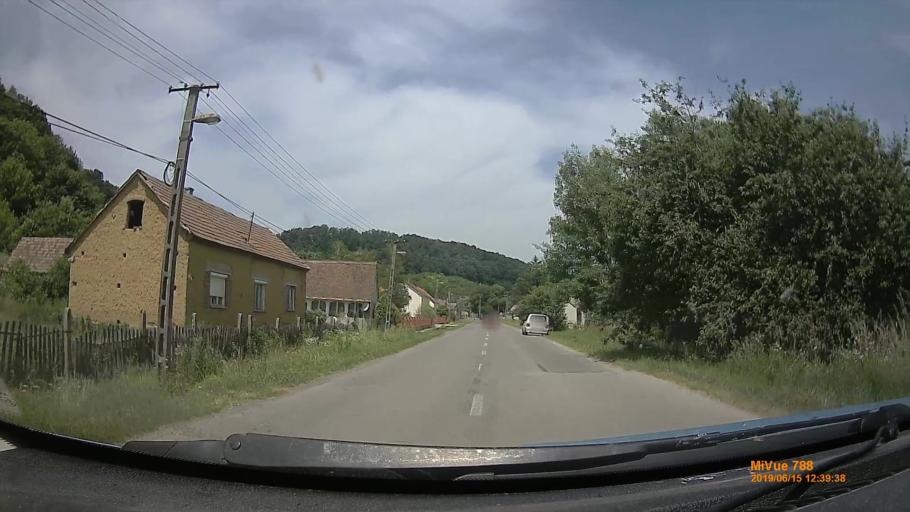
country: HU
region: Baranya
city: Sasd
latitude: 46.1971
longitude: 18.0826
